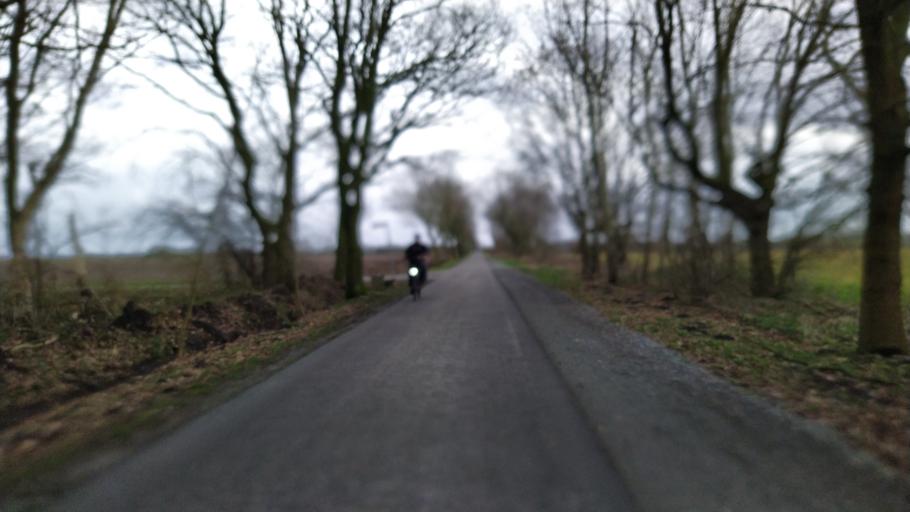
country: DE
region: Lower Saxony
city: Bargstedt
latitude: 53.4468
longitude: 9.4665
